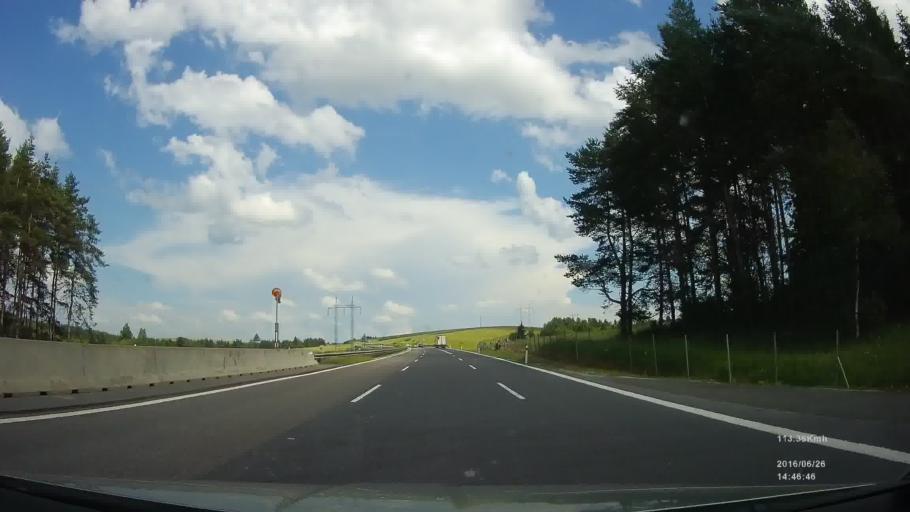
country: SK
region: Presovsky
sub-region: Okres Poprad
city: Strba
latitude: 49.0698
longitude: 20.0198
